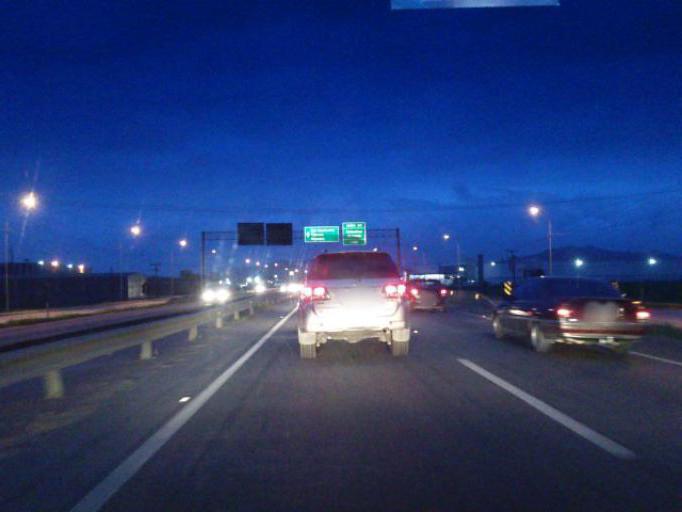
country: BR
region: Santa Catarina
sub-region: Itajai
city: Itajai
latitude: -26.8570
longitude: -48.7274
